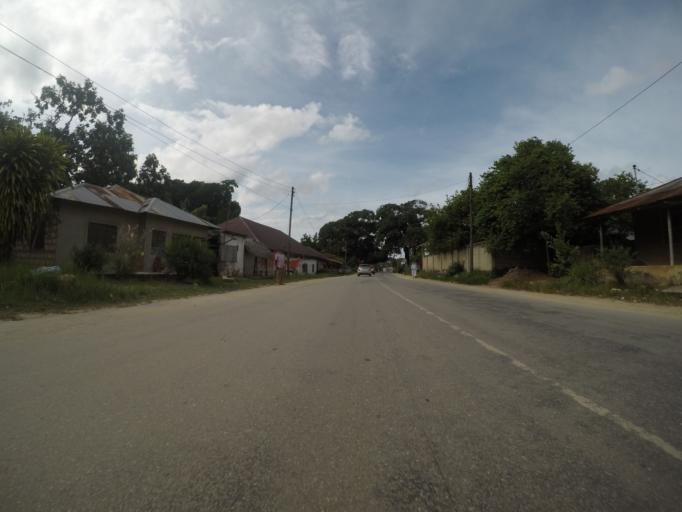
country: TZ
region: Pemba South
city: Chake Chake
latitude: -5.2330
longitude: 39.7765
